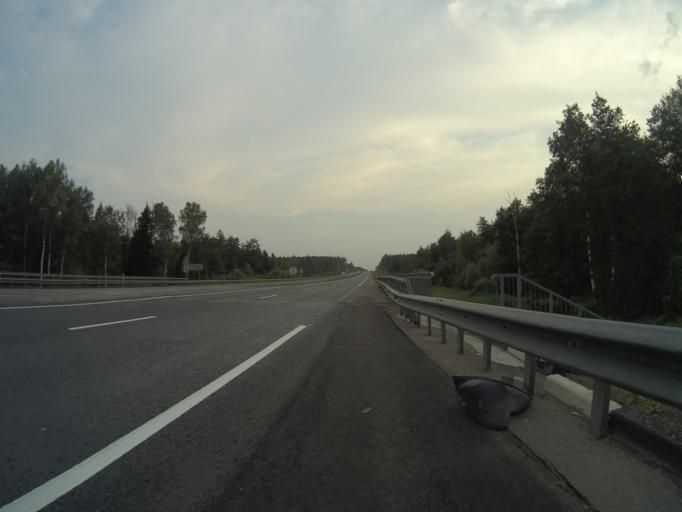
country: RU
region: Vladimir
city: Sudogda
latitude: 56.1241
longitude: 40.8634
